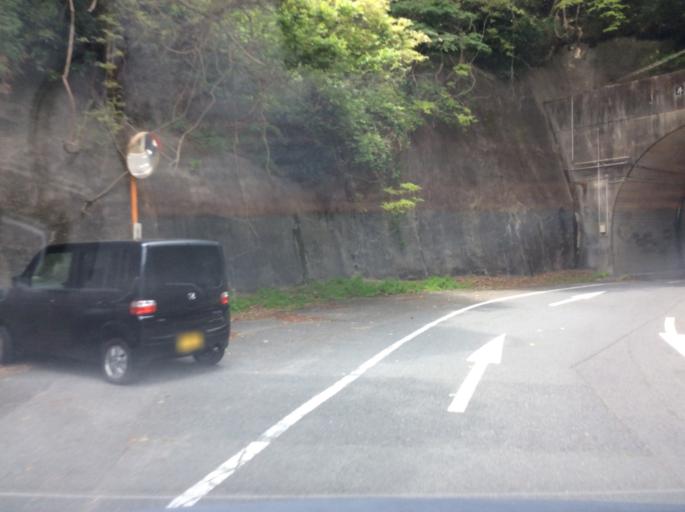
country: JP
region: Ibaraki
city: Kitaibaraki
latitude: 36.8512
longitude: 140.7937
